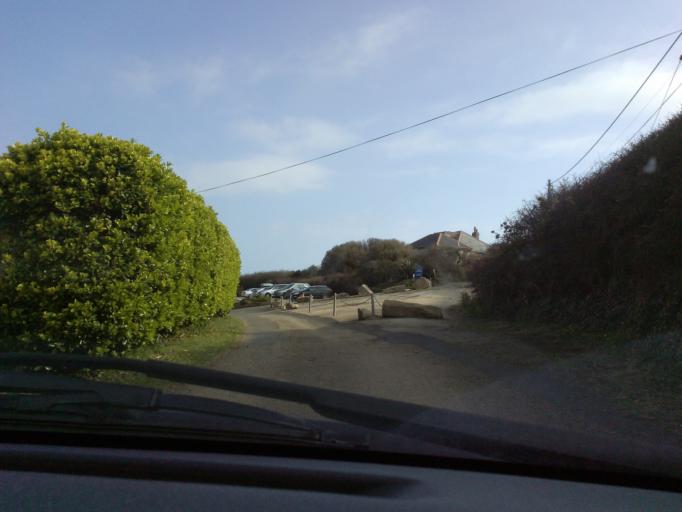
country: GB
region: England
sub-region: Cornwall
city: St. Buryan
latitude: 50.0438
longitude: -5.6544
